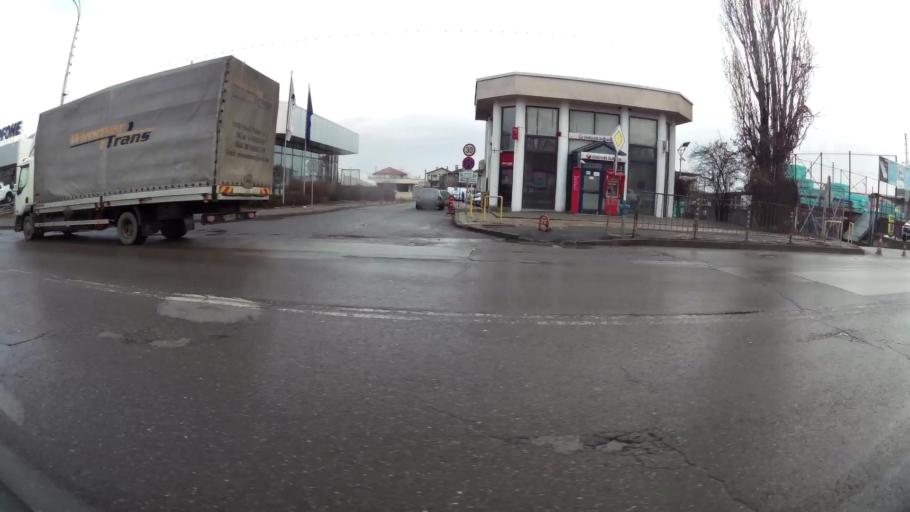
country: BG
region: Sofiya
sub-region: Obshtina Bozhurishte
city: Bozhurishte
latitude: 42.7276
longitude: 23.2607
